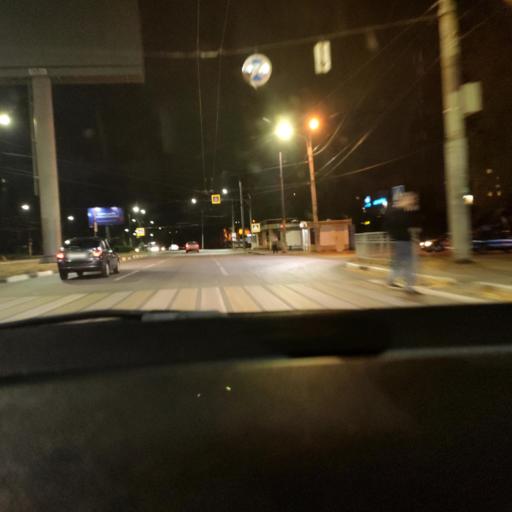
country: RU
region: Voronezj
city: Podgornoye
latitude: 51.7010
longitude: 39.1480
